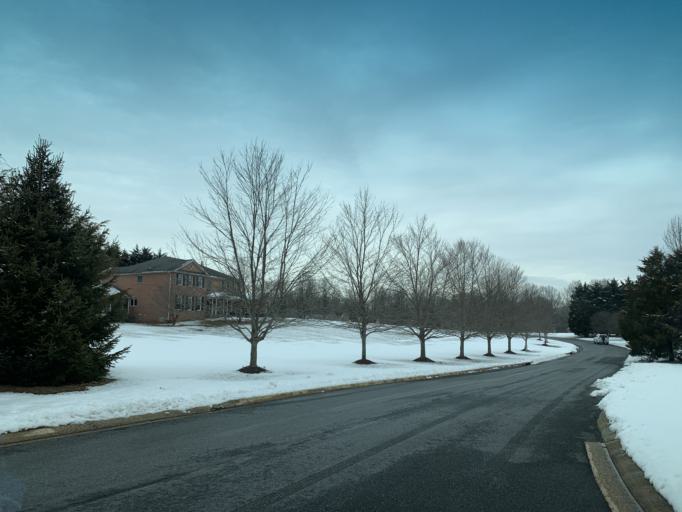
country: US
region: Maryland
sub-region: Harford County
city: Jarrettsville
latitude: 39.5825
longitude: -76.4640
